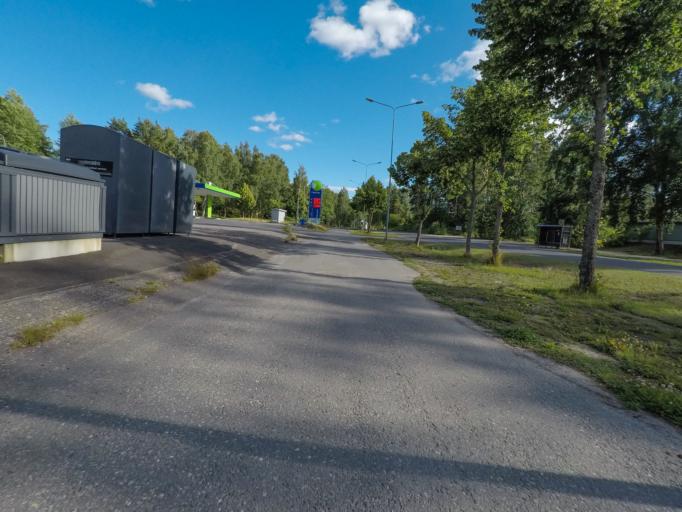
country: FI
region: South Karelia
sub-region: Lappeenranta
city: Lappeenranta
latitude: 61.0776
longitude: 28.1505
